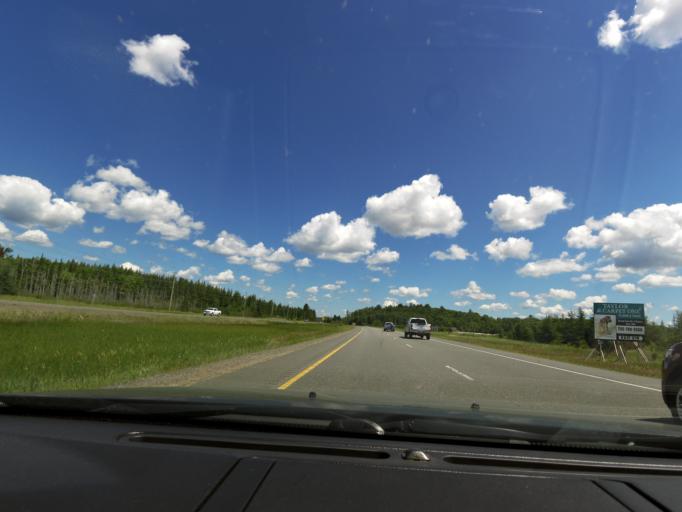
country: CA
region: Ontario
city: Huntsville
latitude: 45.2389
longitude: -79.3006
